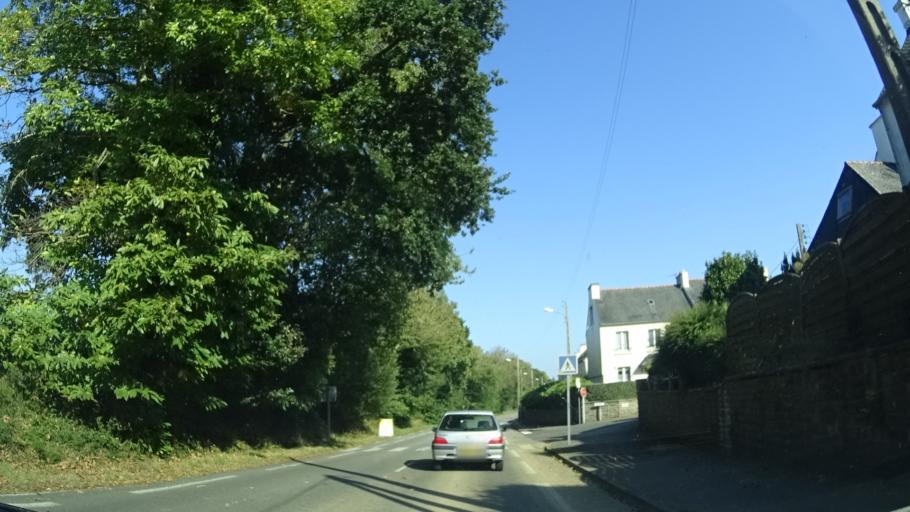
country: FR
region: Brittany
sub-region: Departement du Finistere
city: Douarnenez
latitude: 48.0879
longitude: -4.3158
